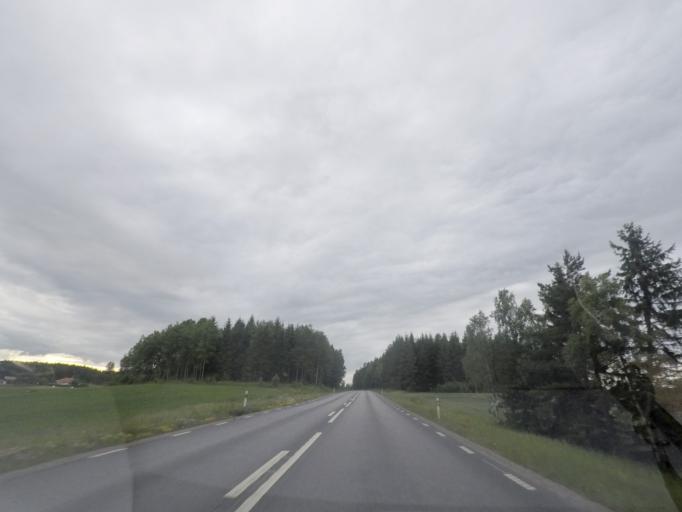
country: SE
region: OErebro
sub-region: Lindesbergs Kommun
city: Lindesberg
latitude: 59.5323
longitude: 15.2682
